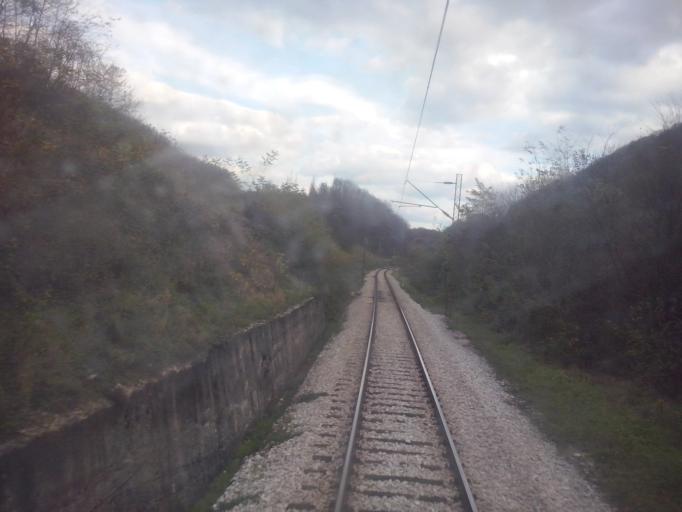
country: RS
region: Central Serbia
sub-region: Zlatiborski Okrug
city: Pozega
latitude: 43.8109
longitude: 19.9882
